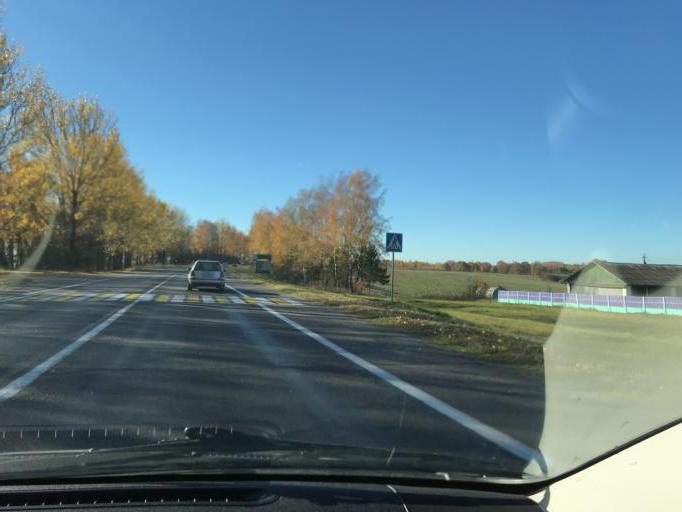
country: BY
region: Vitebsk
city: Lyepyel'
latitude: 54.9271
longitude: 28.7535
